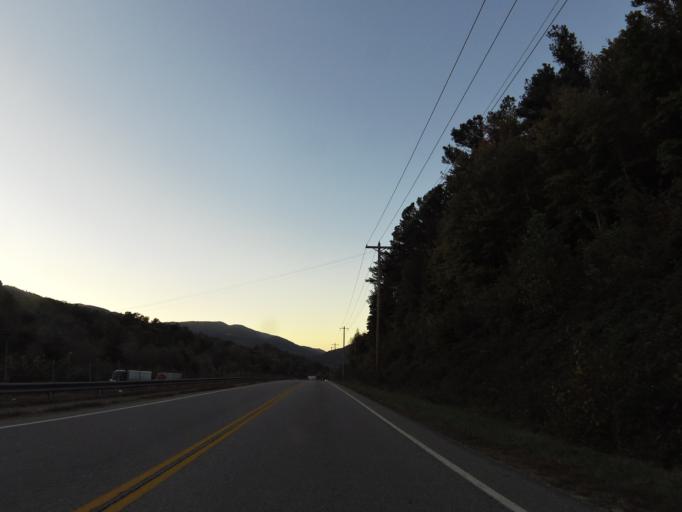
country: US
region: Tennessee
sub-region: Campbell County
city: Caryville
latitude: 36.2833
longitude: -84.2102
